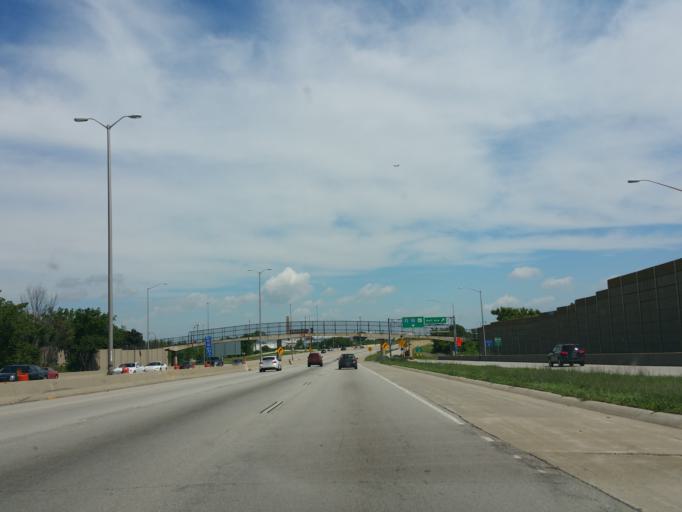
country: US
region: Wisconsin
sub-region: Milwaukee County
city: Saint Francis
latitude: 42.9777
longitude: -87.9157
